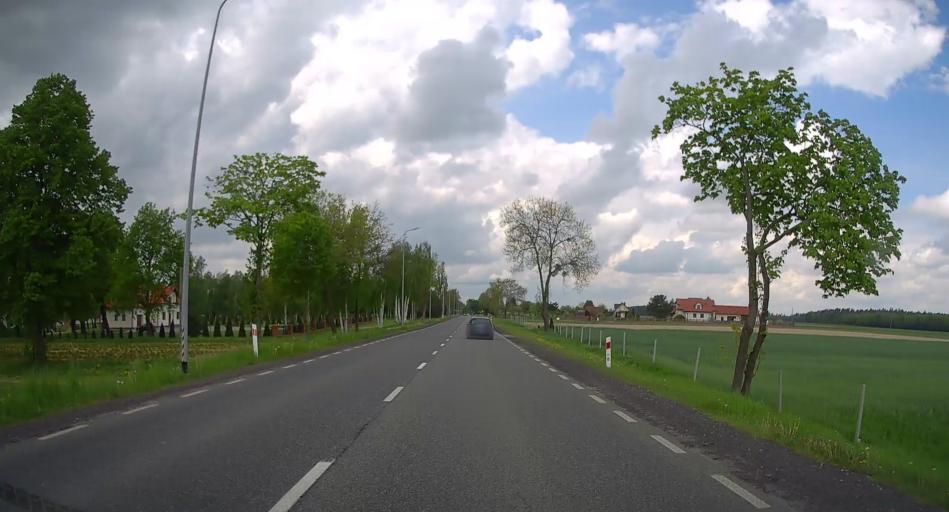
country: PL
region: Masovian Voivodeship
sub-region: Powiat plonski
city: Zaluski
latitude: 52.4460
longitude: 20.5095
